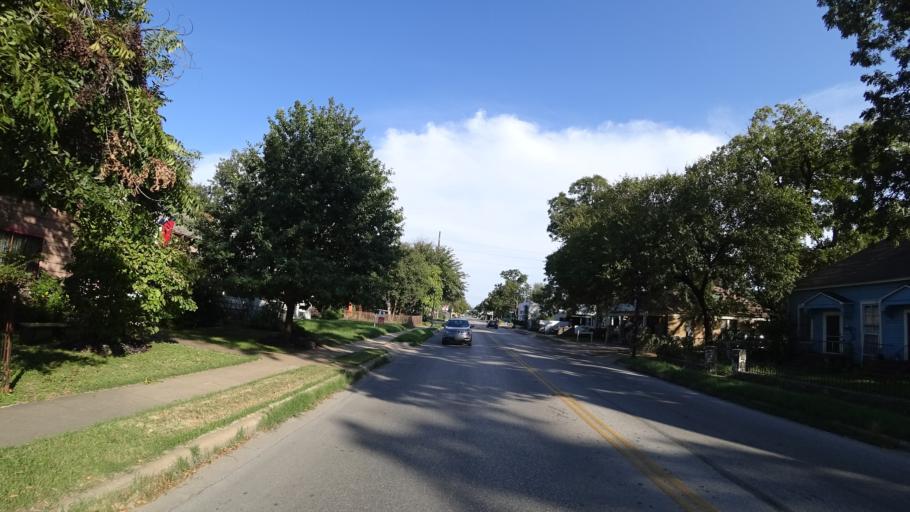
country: US
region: Texas
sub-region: Travis County
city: Austin
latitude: 30.2595
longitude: -97.7314
